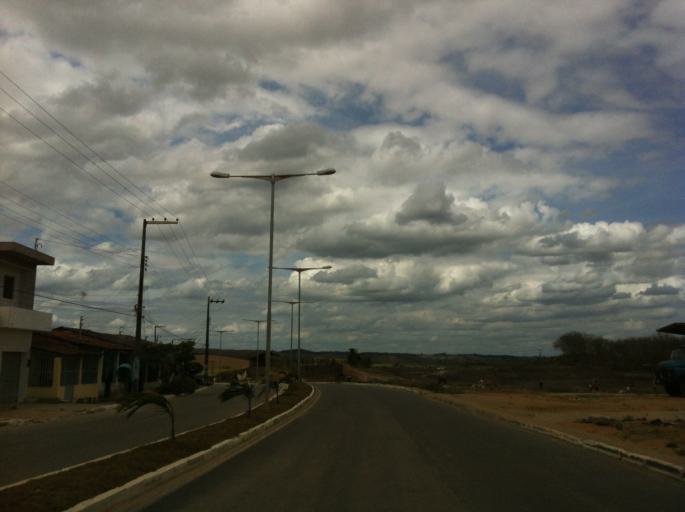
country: BR
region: Alagoas
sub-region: Ibateguara
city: Ibateguara
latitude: -8.9668
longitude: -35.9218
